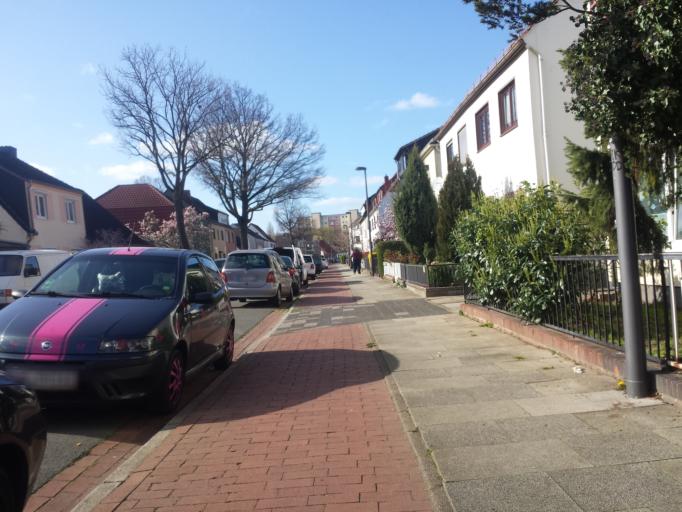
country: DE
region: Lower Saxony
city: Lilienthal
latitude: 53.0606
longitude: 8.8946
